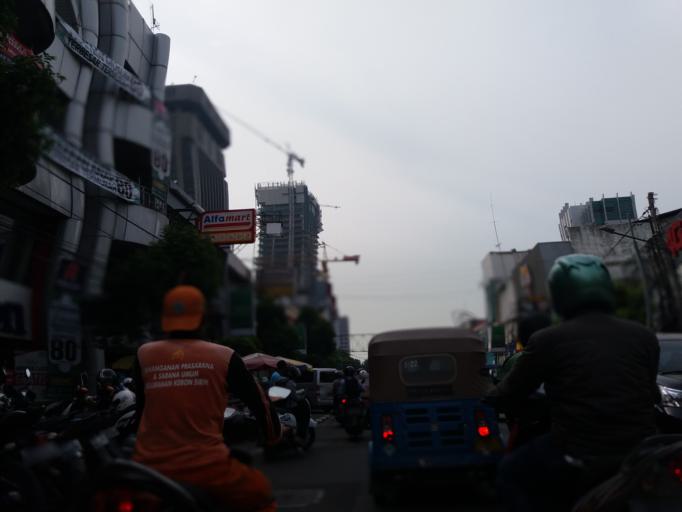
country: ID
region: Jakarta Raya
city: Jakarta
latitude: -6.1857
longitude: 106.8251
